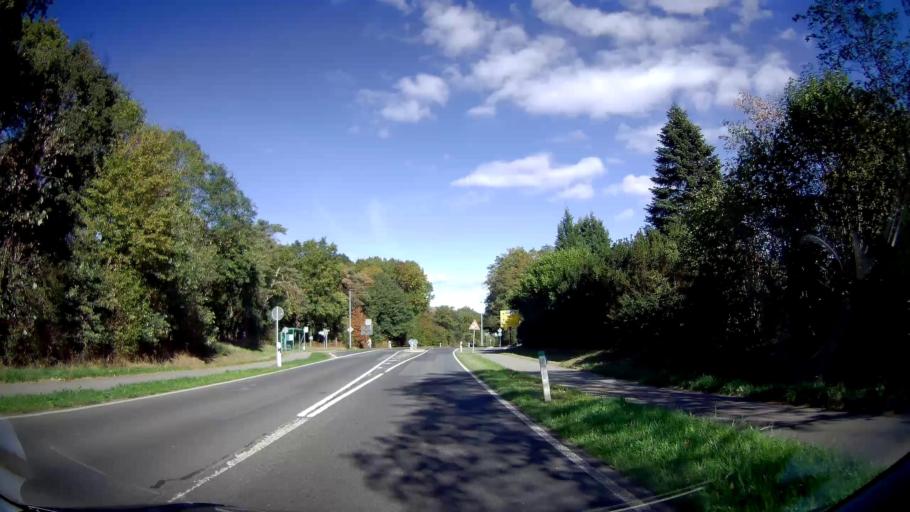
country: DE
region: North Rhine-Westphalia
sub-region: Regierungsbezirk Dusseldorf
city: Hunxe
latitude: 51.6280
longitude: 6.7582
